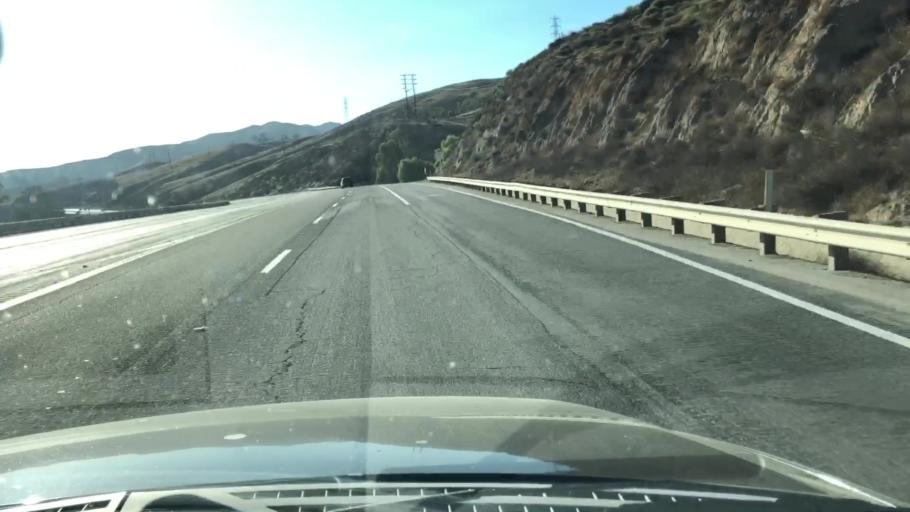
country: US
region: California
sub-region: Los Angeles County
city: Val Verde
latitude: 34.4245
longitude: -118.6446
